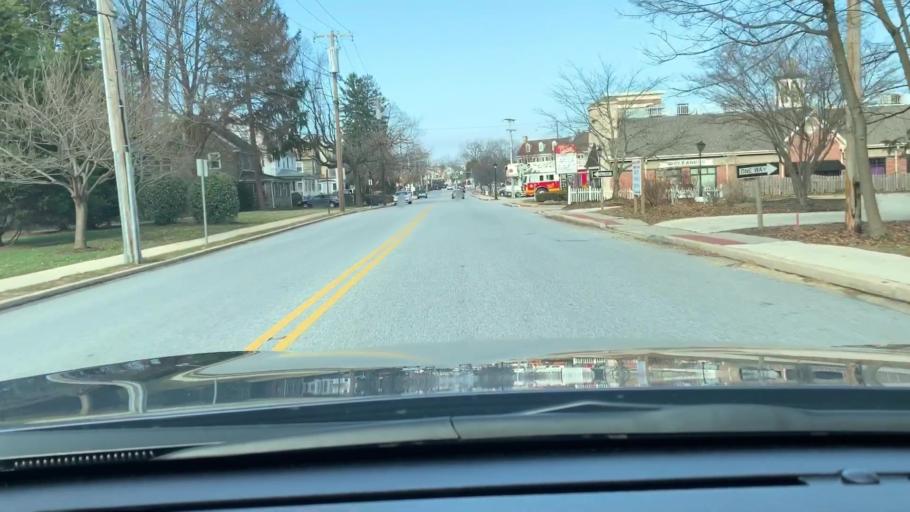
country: US
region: Pennsylvania
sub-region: Chester County
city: Paoli
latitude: 40.0397
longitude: -75.4809
